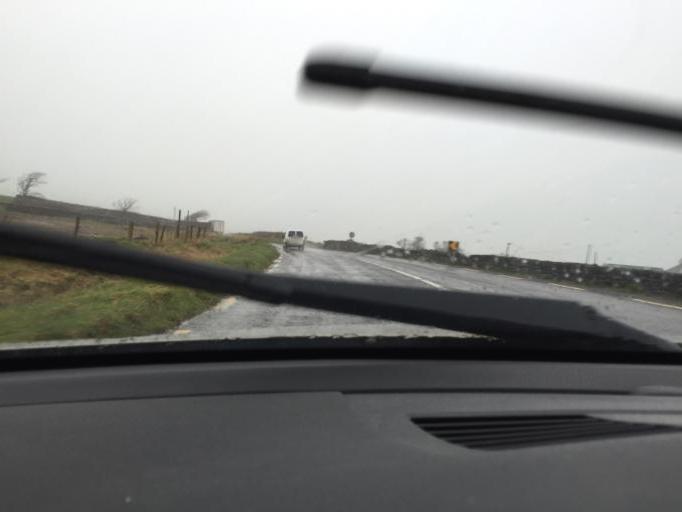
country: IE
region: Munster
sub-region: Ciarrai
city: Dingle
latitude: 52.1298
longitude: -10.2455
